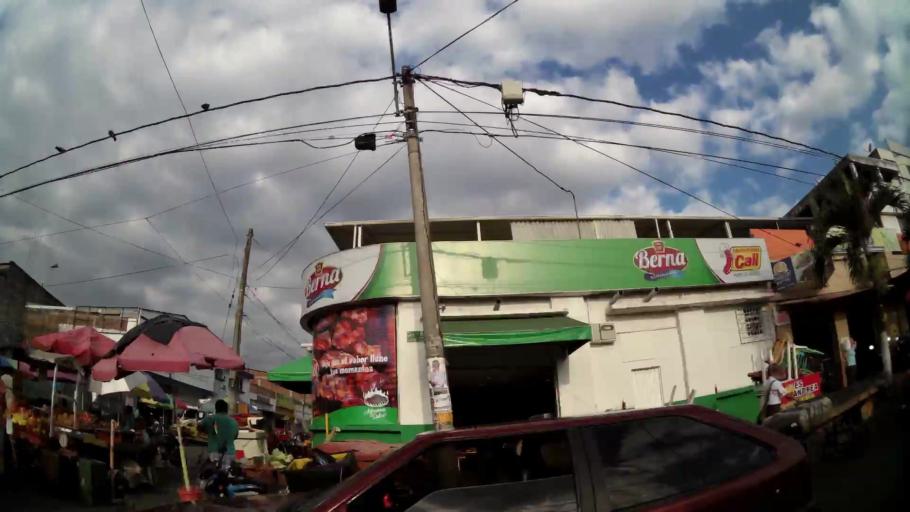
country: CO
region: Valle del Cauca
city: Cali
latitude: 3.4349
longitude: -76.5360
